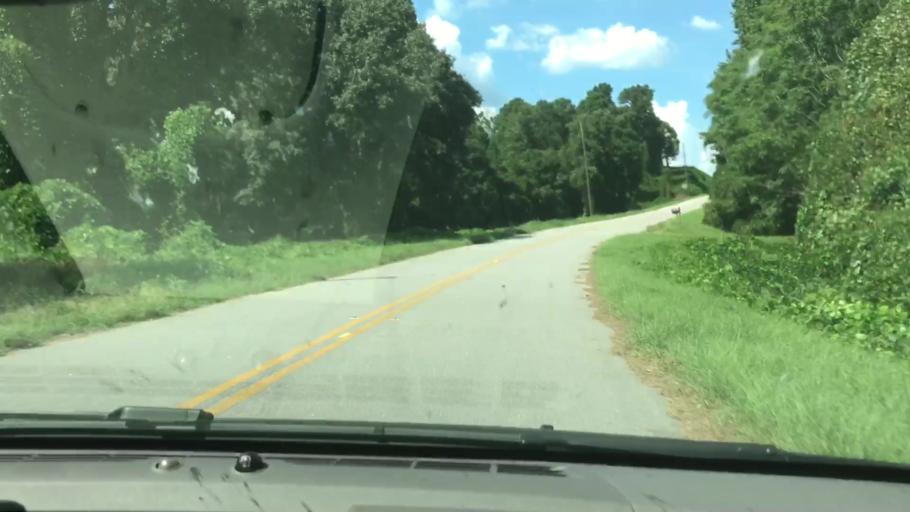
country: US
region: Georgia
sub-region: Troup County
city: La Grange
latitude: 33.0765
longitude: -85.1305
